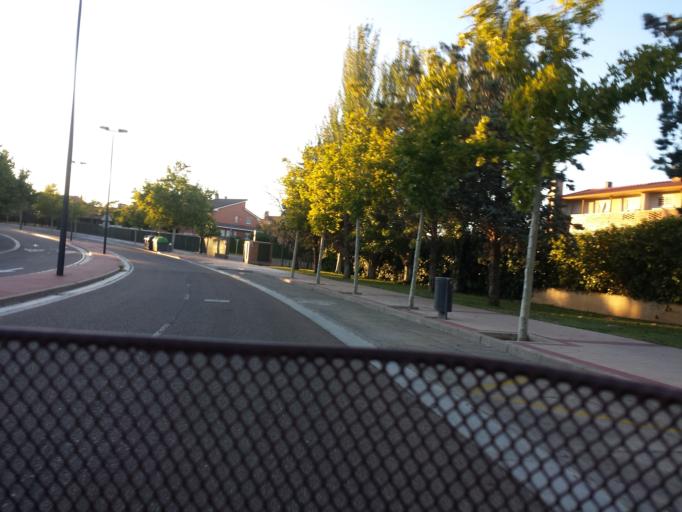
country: ES
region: Aragon
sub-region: Provincia de Zaragoza
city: Montecanal
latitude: 41.6308
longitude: -0.9367
